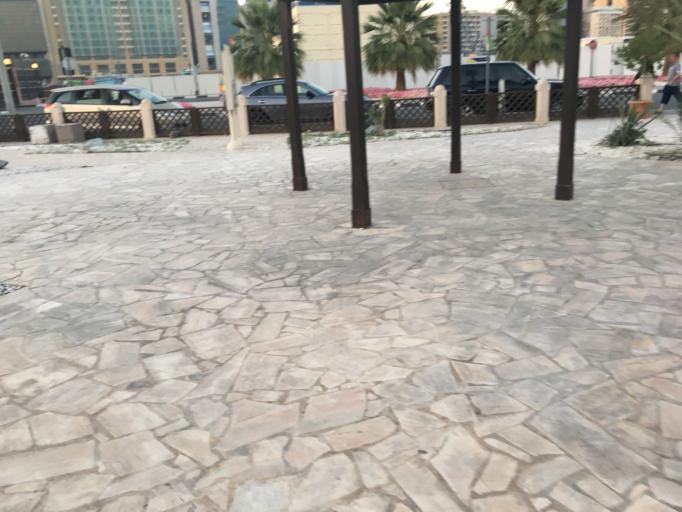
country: AE
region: Ash Shariqah
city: Sharjah
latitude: 25.2647
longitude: 55.3008
